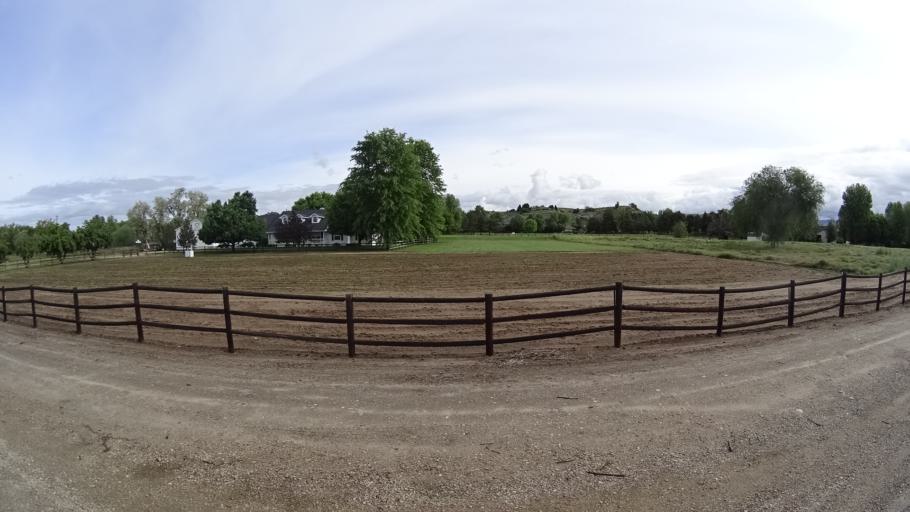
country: US
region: Idaho
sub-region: Ada County
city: Eagle
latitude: 43.7208
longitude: -116.3324
